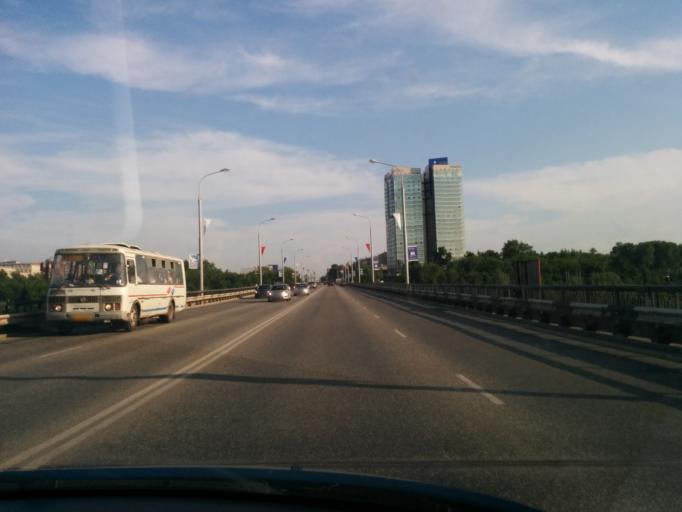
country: RU
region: Perm
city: Perm
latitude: 58.0185
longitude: 56.2218
